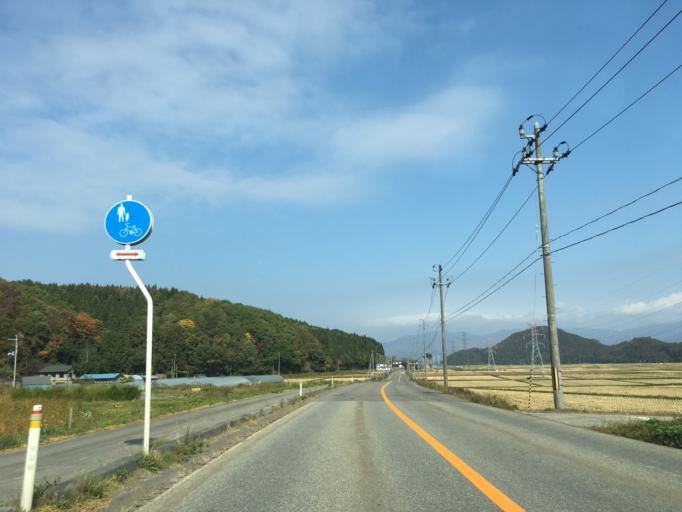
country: JP
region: Fukushima
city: Inawashiro
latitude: 37.4802
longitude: 140.0104
